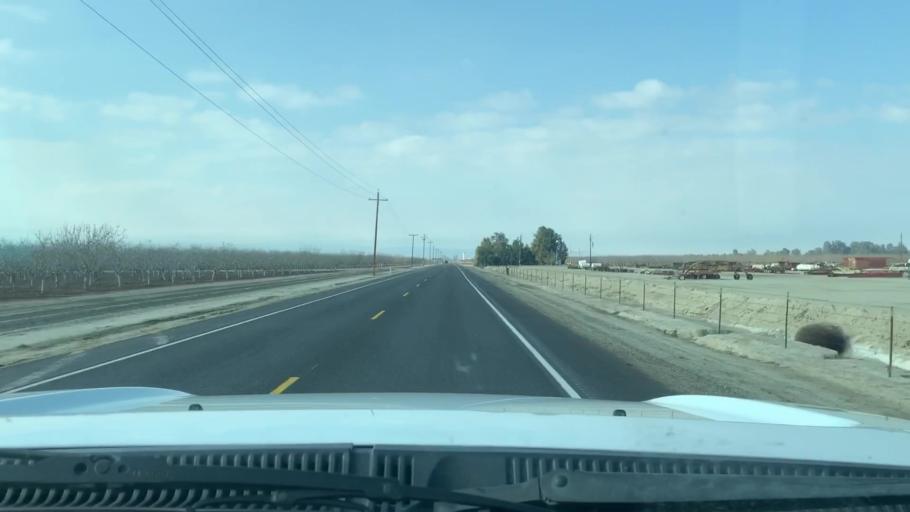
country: US
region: California
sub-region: Kern County
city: Buttonwillow
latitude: 35.4423
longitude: -119.4184
